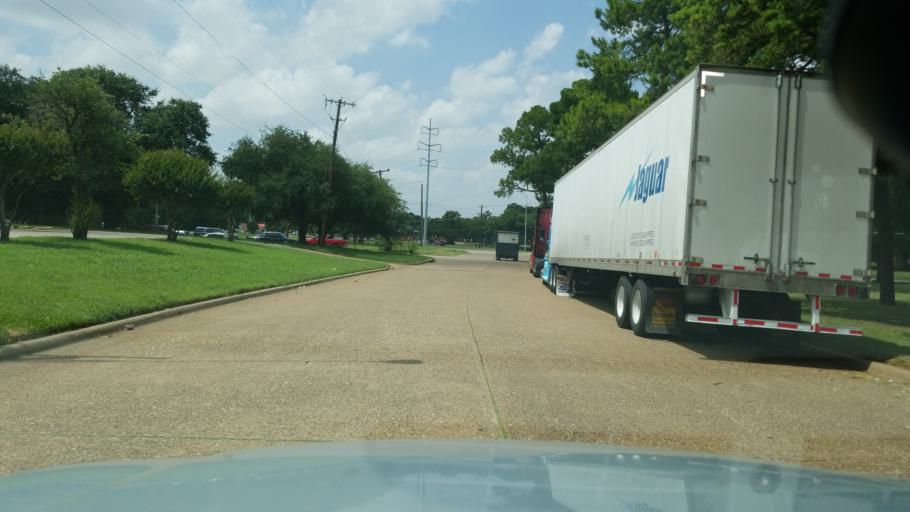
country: US
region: Texas
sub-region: Dallas County
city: University Park
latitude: 32.8309
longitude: -96.8598
